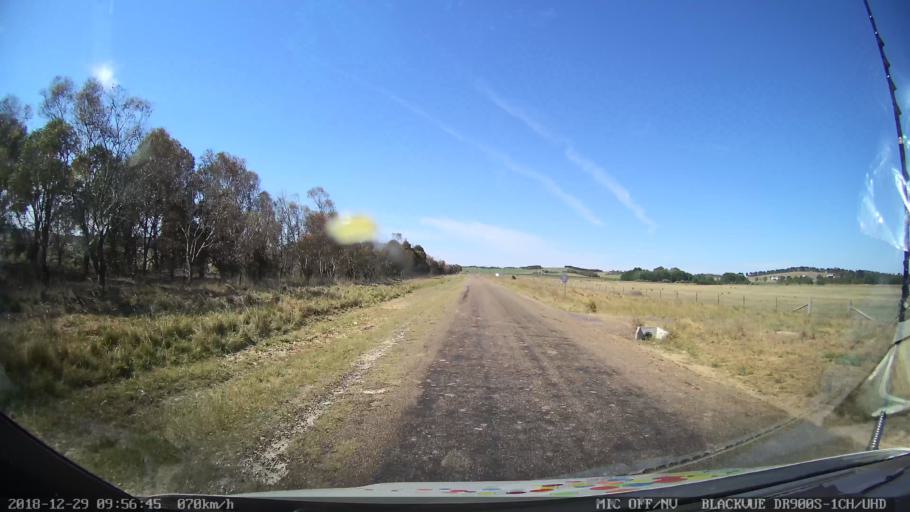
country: AU
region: New South Wales
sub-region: Goulburn Mulwaree
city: Goulburn
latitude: -34.7801
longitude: 149.4817
